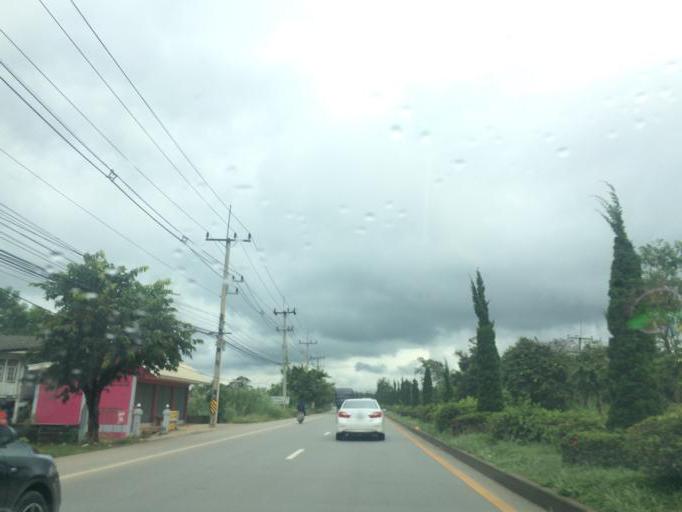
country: TH
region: Chiang Rai
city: Mae Chan
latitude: 20.0279
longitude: 99.8730
